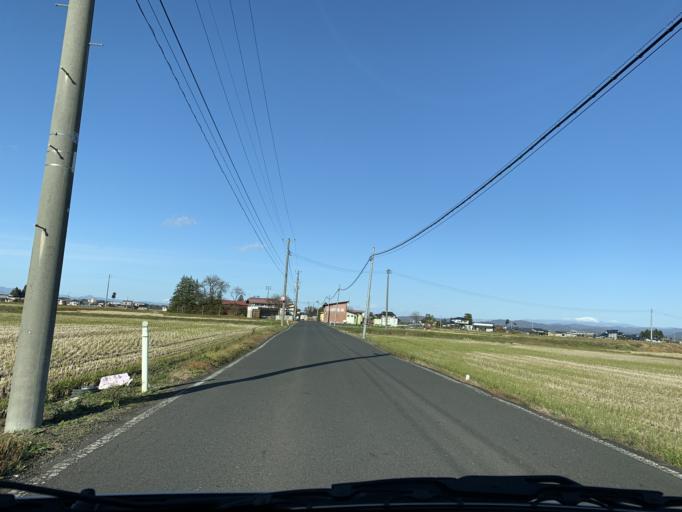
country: JP
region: Iwate
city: Mizusawa
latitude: 39.1556
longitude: 141.0973
